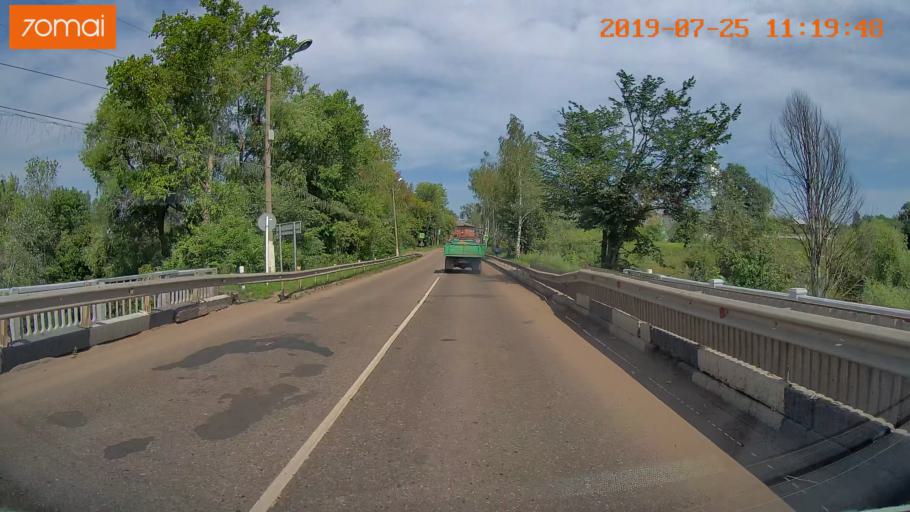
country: RU
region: Ivanovo
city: Privolzhsk
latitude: 57.3768
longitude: 41.2795
